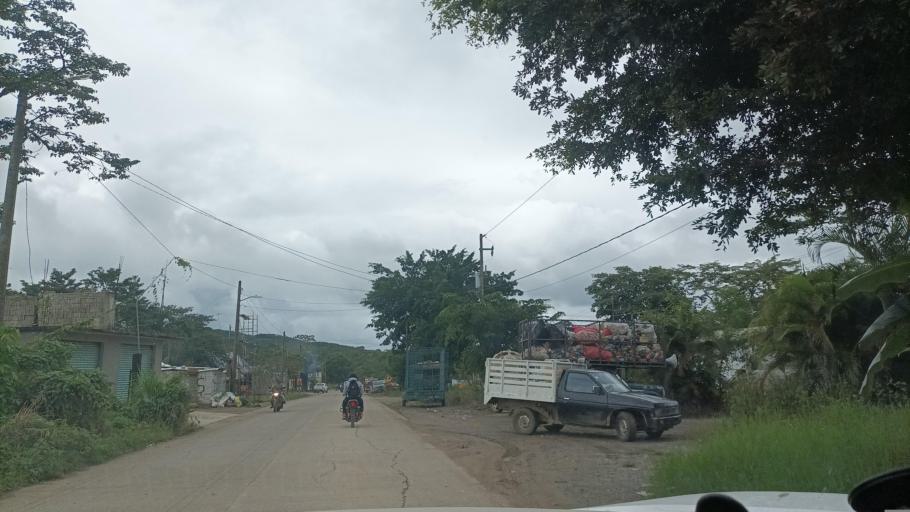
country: MX
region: Veracruz
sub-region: Uxpanapa
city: Poblado 10
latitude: 17.2783
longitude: -94.4570
